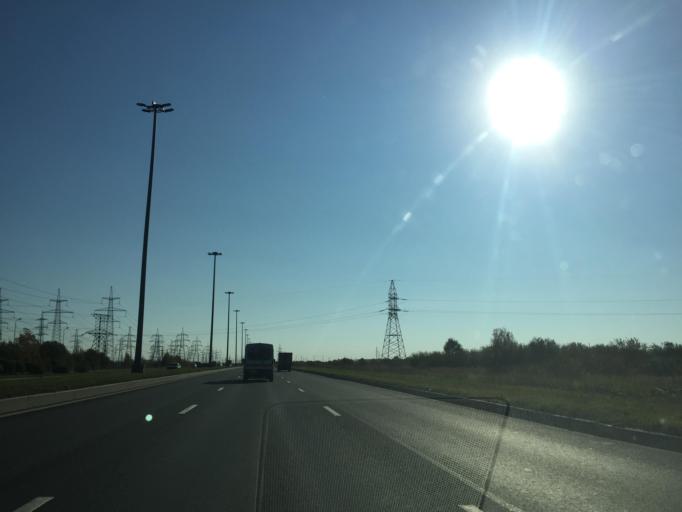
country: RU
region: St.-Petersburg
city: Petro-Slavyanka
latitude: 59.7596
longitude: 30.5131
